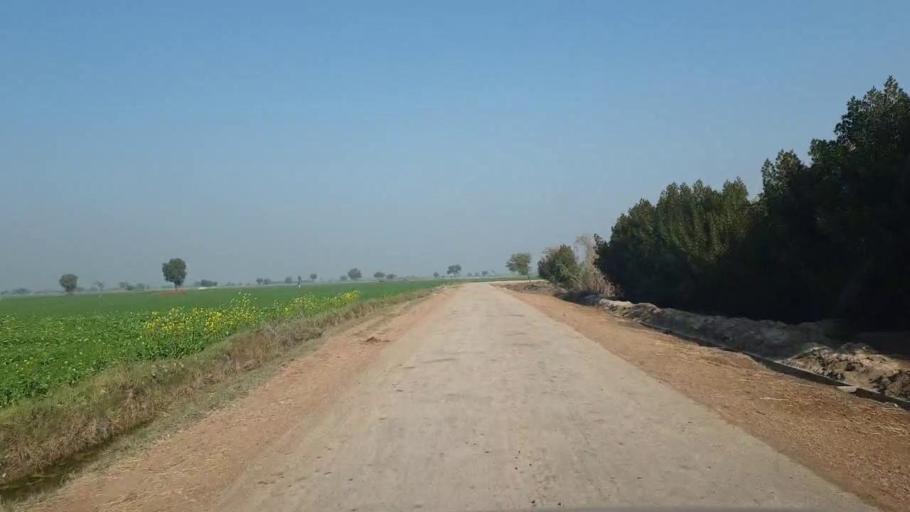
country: PK
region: Sindh
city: Shahdadpur
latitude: 25.9745
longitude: 68.5876
